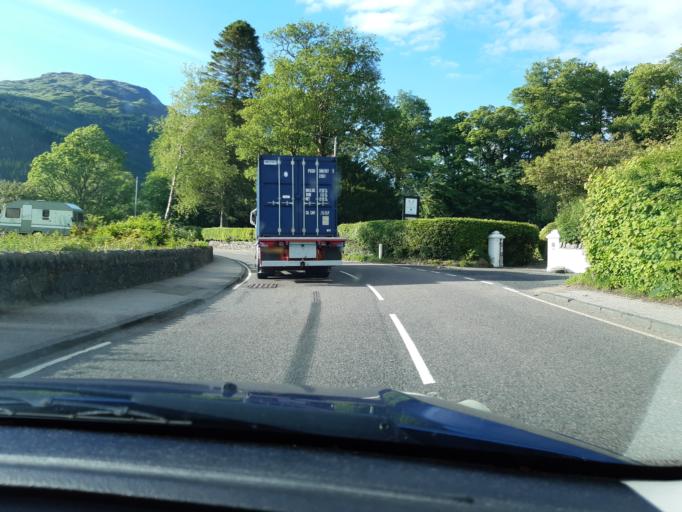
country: GB
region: Scotland
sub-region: Argyll and Bute
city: Garelochhead
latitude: 56.2046
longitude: -4.7435
